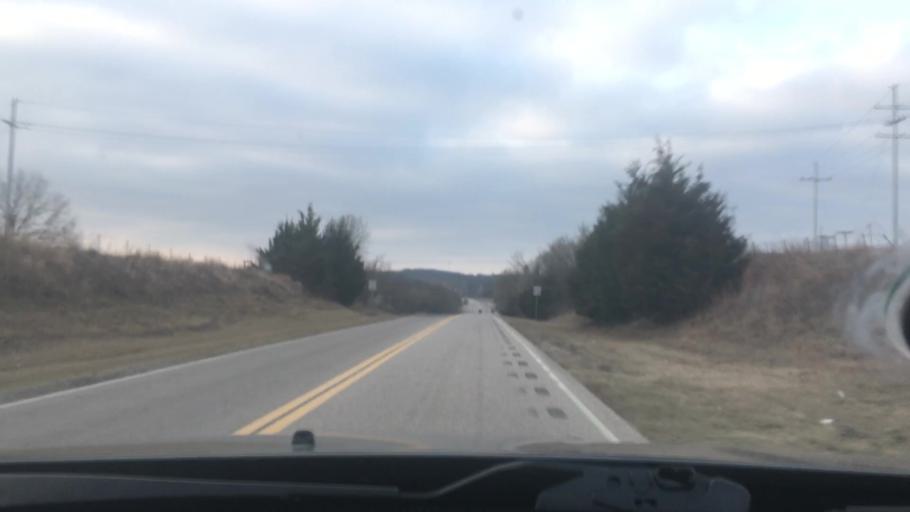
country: US
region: Oklahoma
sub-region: Pontotoc County
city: Ada
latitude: 34.6206
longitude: -96.6349
